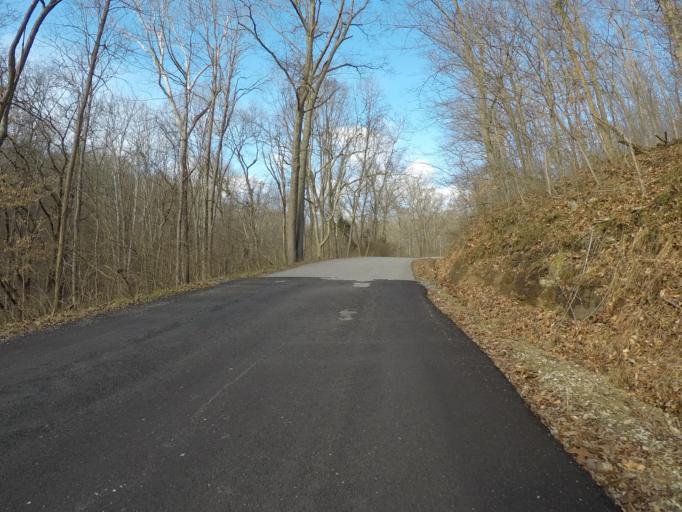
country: US
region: West Virginia
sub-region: Cabell County
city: Pea Ridge
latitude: 38.4283
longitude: -82.3391
